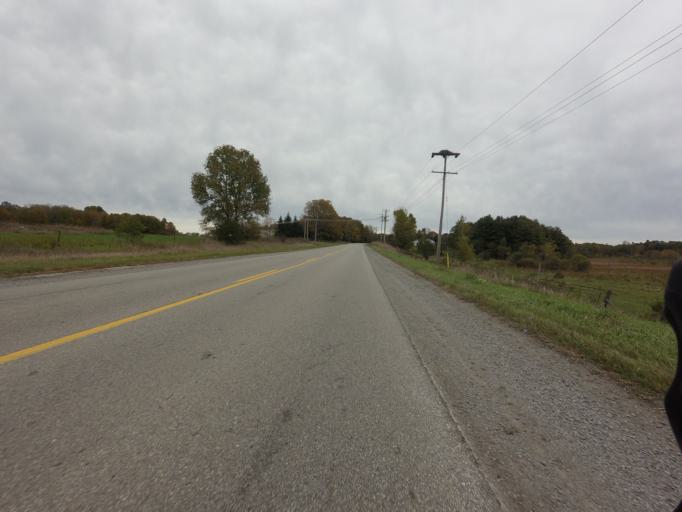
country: CA
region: Ontario
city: Gananoque
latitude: 44.5600
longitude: -76.1159
